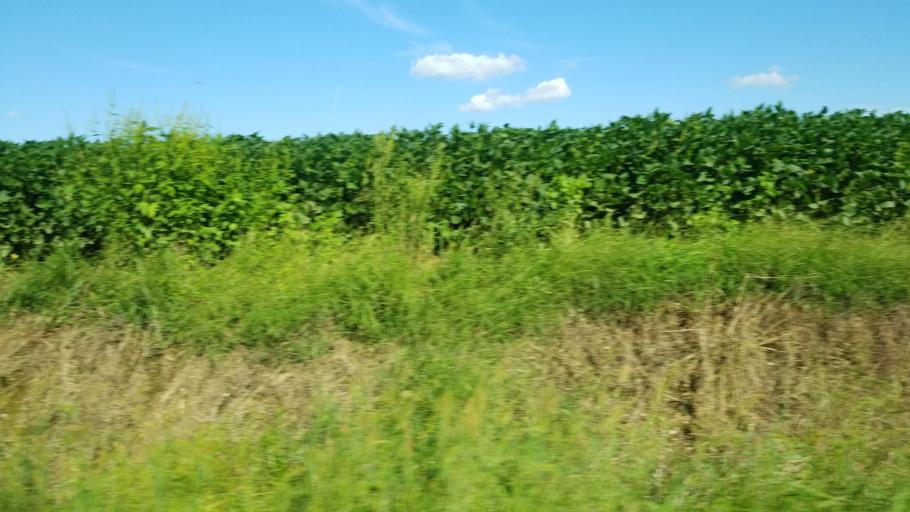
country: US
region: Illinois
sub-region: Saline County
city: Harrisburg
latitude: 37.8219
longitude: -88.5672
